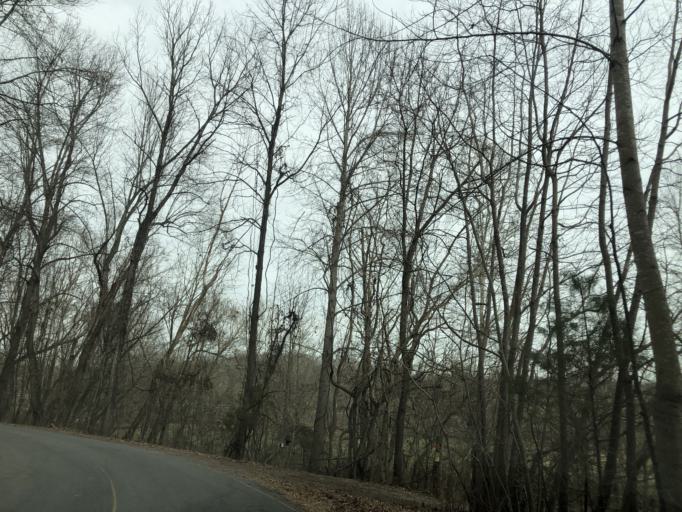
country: US
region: Tennessee
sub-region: Robertson County
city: Greenbrier
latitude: 36.4825
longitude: -86.7927
